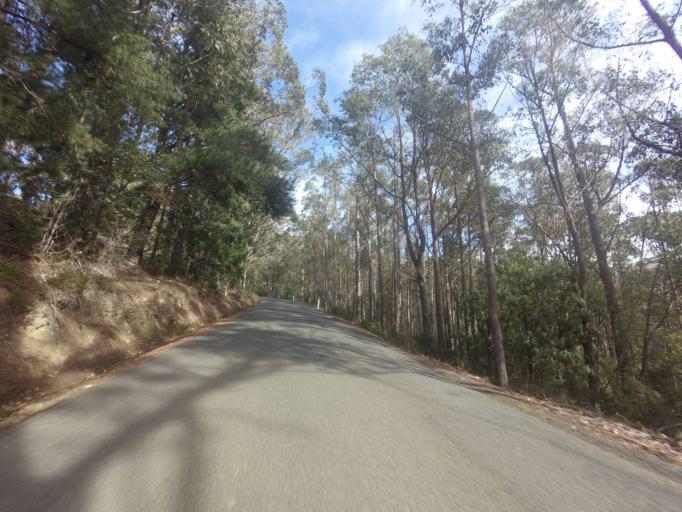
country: AU
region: Tasmania
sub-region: Kingborough
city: Margate
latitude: -43.0082
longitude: 147.1687
